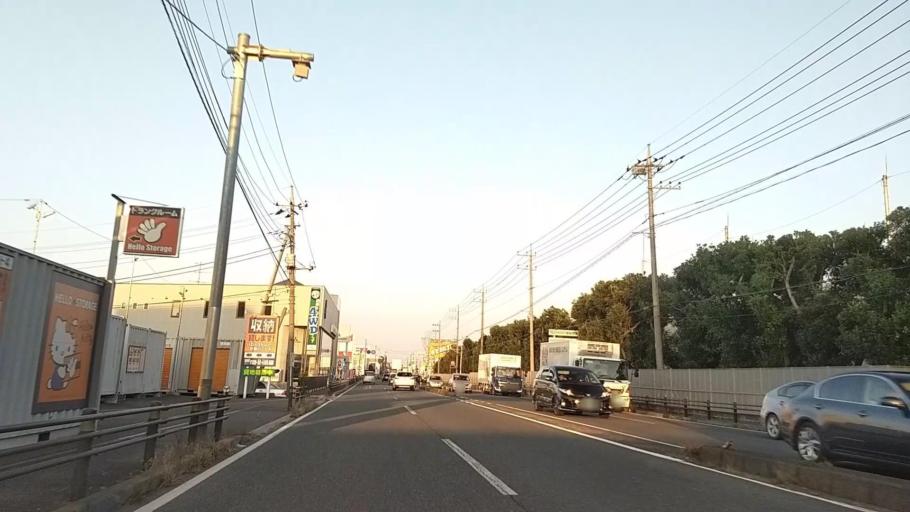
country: JP
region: Saitama
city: Kawagoe
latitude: 35.8897
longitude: 139.4477
